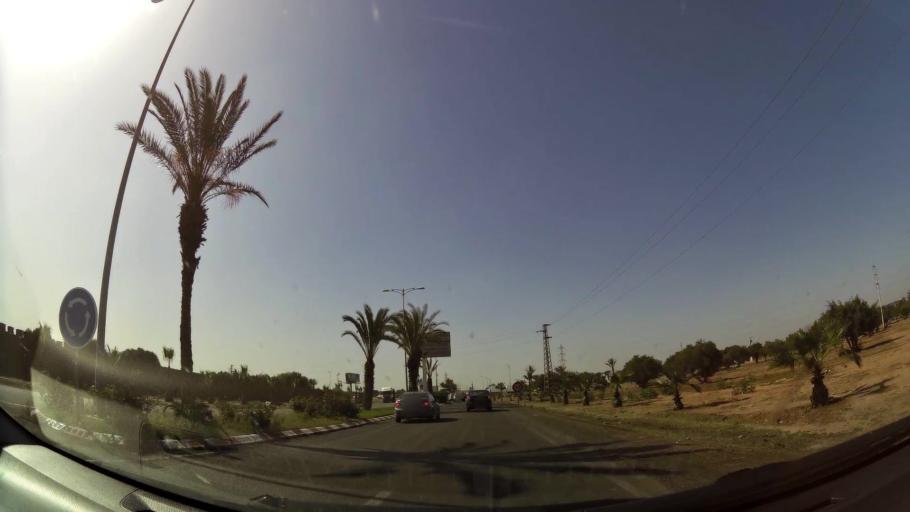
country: MA
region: Souss-Massa-Draa
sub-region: Inezgane-Ait Mellou
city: Inezgane
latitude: 30.3414
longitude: -9.4786
